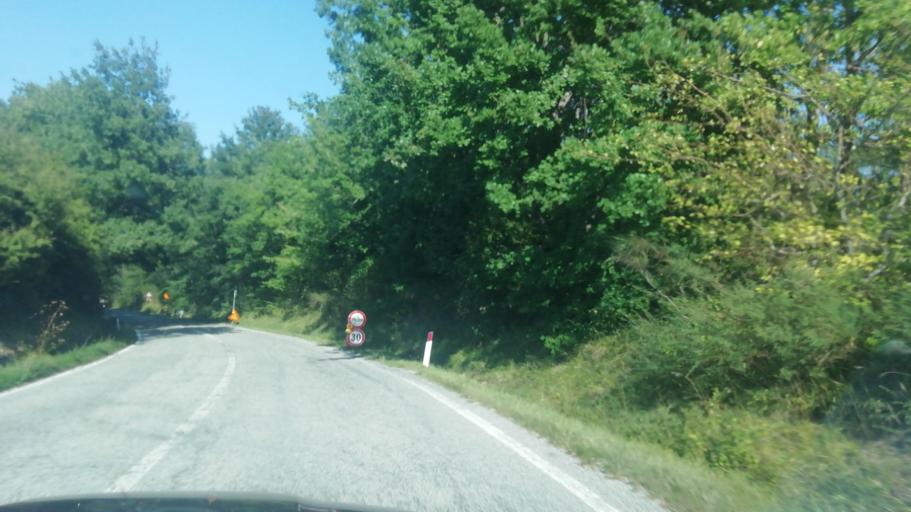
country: IT
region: The Marches
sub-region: Provincia di Pesaro e Urbino
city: Frontone
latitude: 43.5403
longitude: 12.7136
